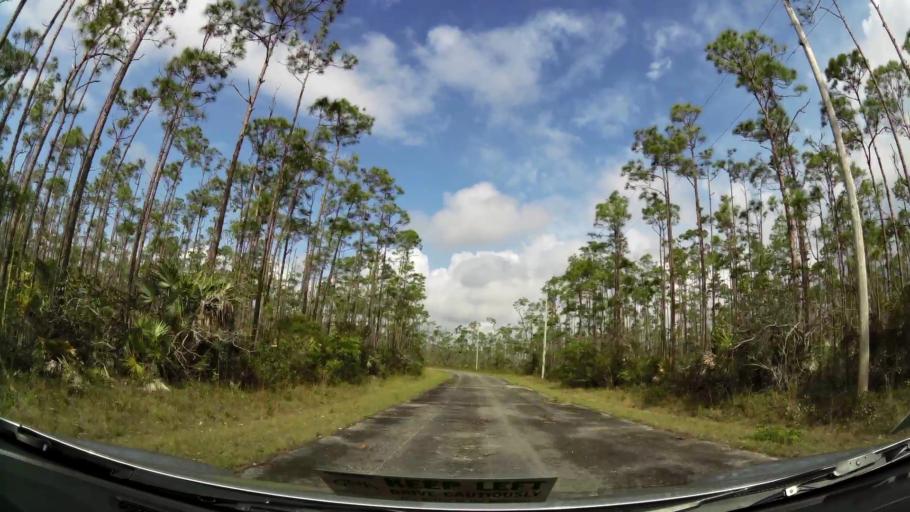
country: BS
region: Freeport
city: Lucaya
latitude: 26.5796
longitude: -78.5531
